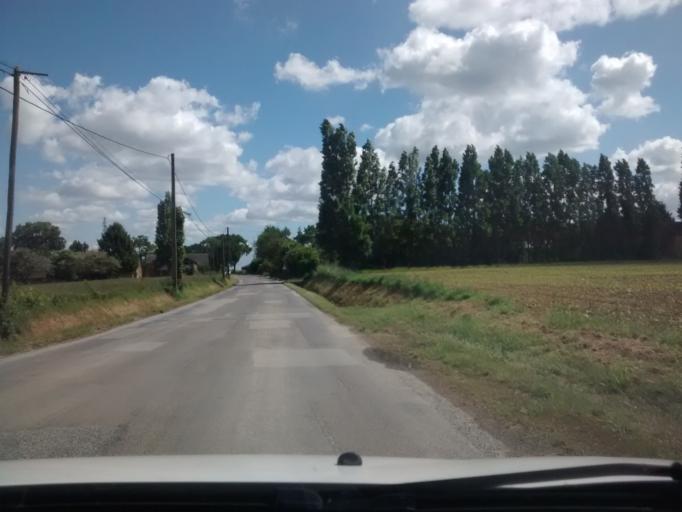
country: FR
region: Brittany
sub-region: Departement d'Ille-et-Vilaine
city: Cesson-Sevigne
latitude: 48.1446
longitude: -1.6070
